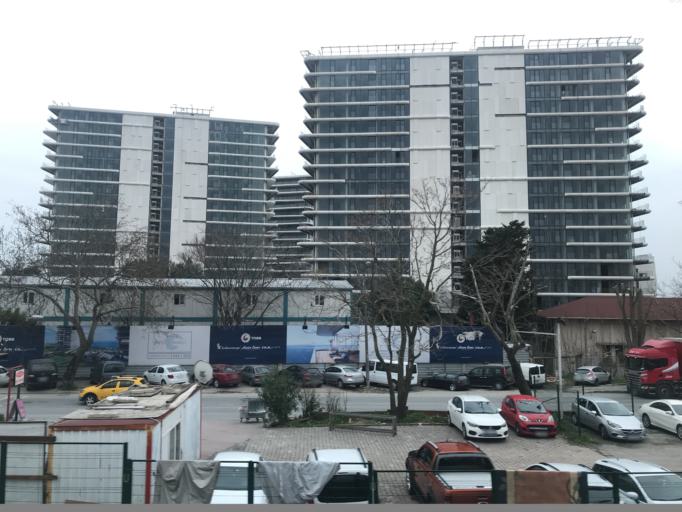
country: TR
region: Istanbul
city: Zeytinburnu
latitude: 40.9830
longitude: 28.9015
